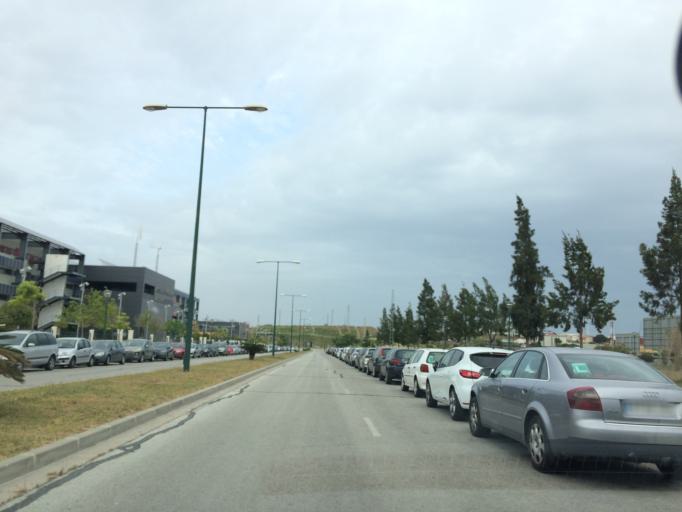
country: ES
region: Andalusia
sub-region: Provincia de Malaga
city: Malaga
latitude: 36.7148
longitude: -4.4940
